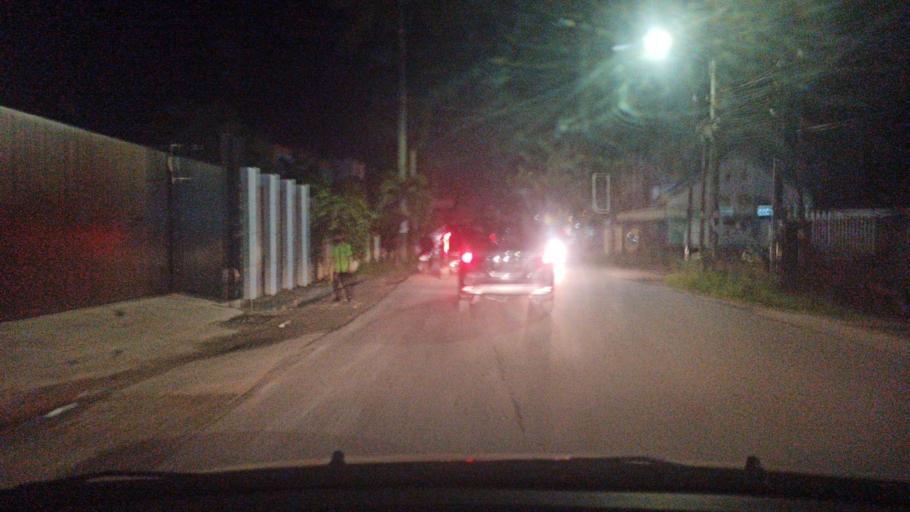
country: ID
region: South Sumatra
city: Palembang
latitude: -2.9424
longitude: 104.7839
